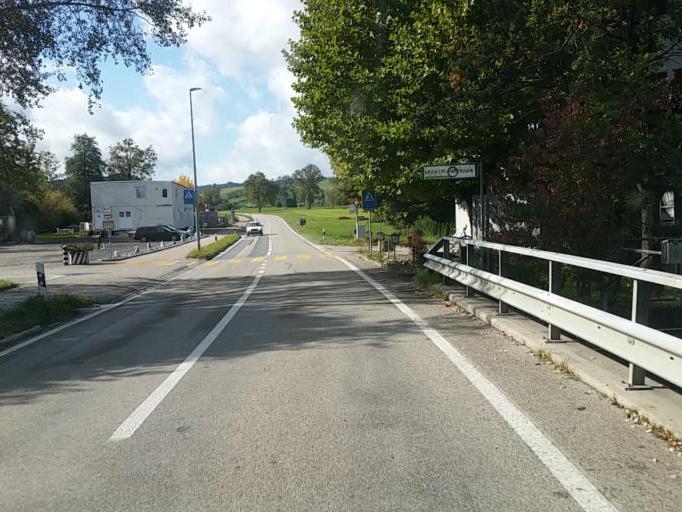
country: CH
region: Bern
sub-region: Oberaargau
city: Madiswil
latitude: 47.1483
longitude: 7.7843
